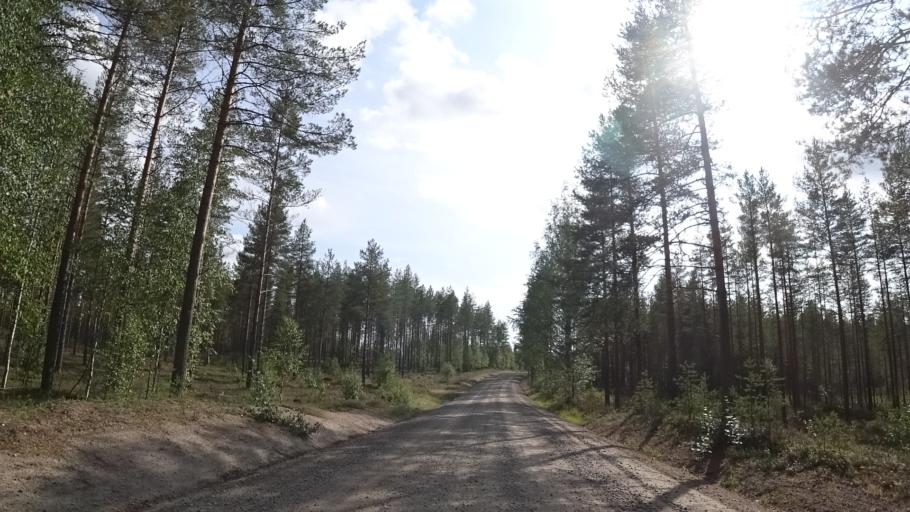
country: FI
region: North Karelia
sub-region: Pielisen Karjala
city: Lieksa
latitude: 63.5565
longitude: 30.0644
